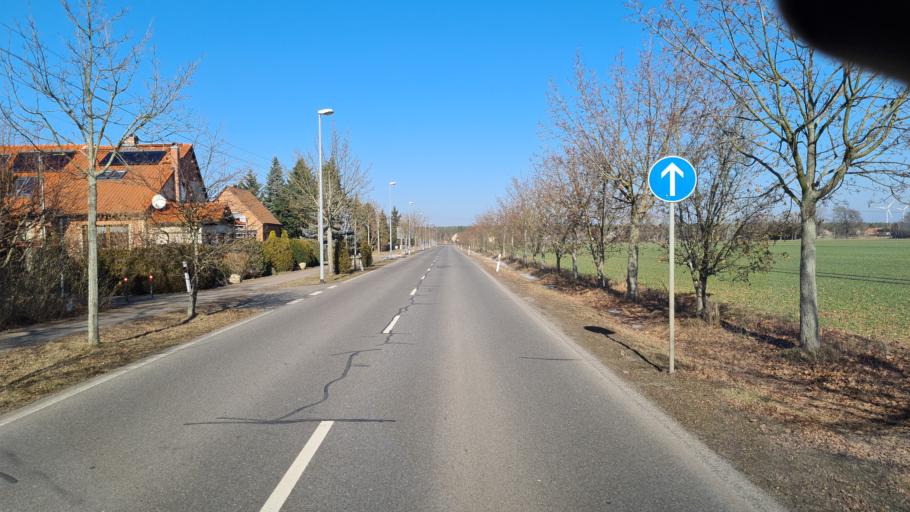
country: DE
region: Brandenburg
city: Grossraschen
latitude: 51.5811
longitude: 14.0323
